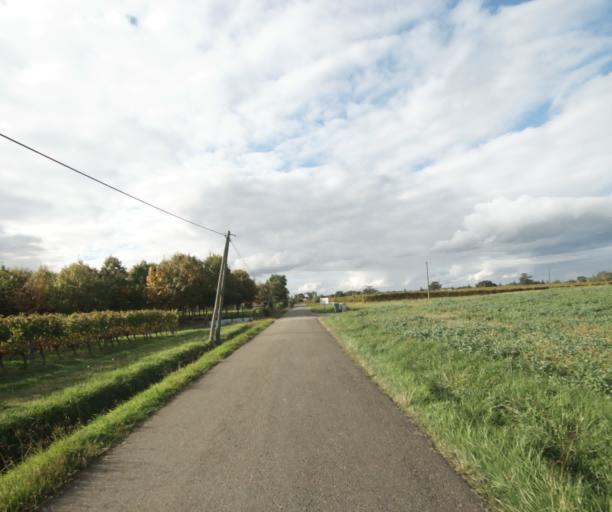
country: FR
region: Midi-Pyrenees
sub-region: Departement du Gers
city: Eauze
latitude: 43.8813
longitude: 0.0783
